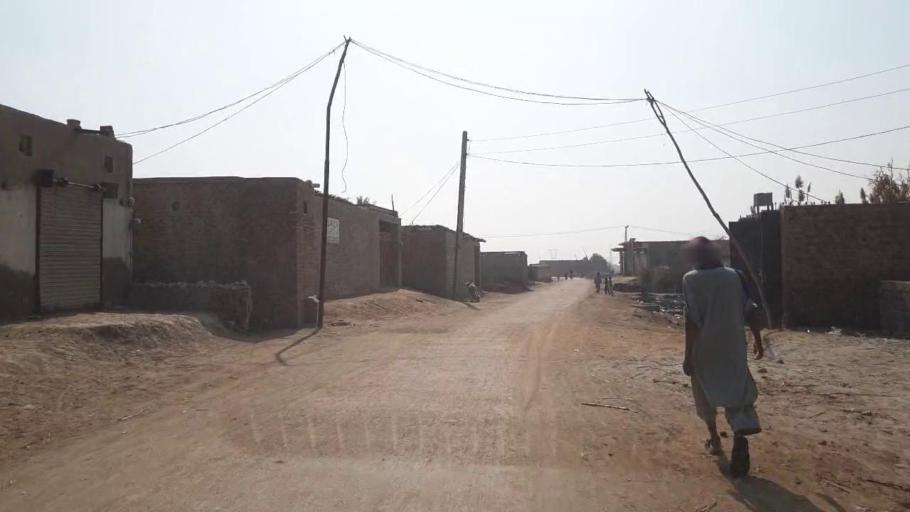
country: PK
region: Sindh
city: Bhit Shah
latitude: 25.7052
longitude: 68.5448
